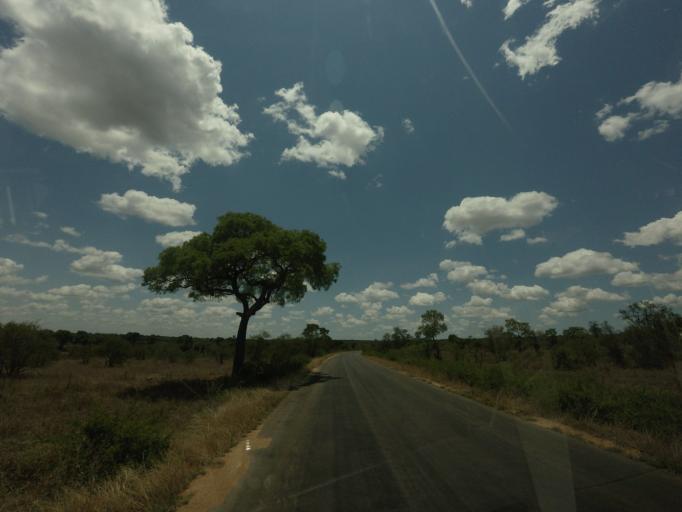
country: ZA
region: Limpopo
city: Thulamahashi
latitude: -24.6919
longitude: 31.8144
